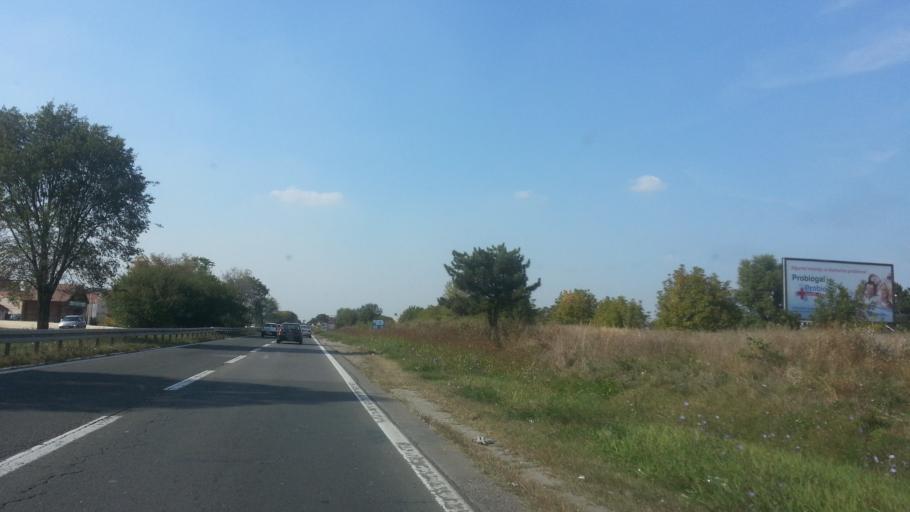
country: RS
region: Central Serbia
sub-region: Belgrade
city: Zemun
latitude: 44.8586
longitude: 20.3584
